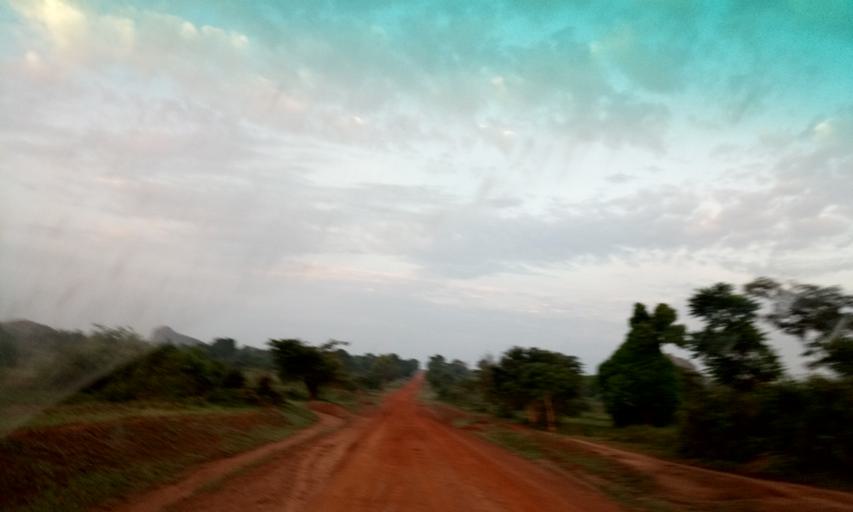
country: UG
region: Eastern Region
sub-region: Ngora District
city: Ngora
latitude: 1.4672
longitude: 33.8119
